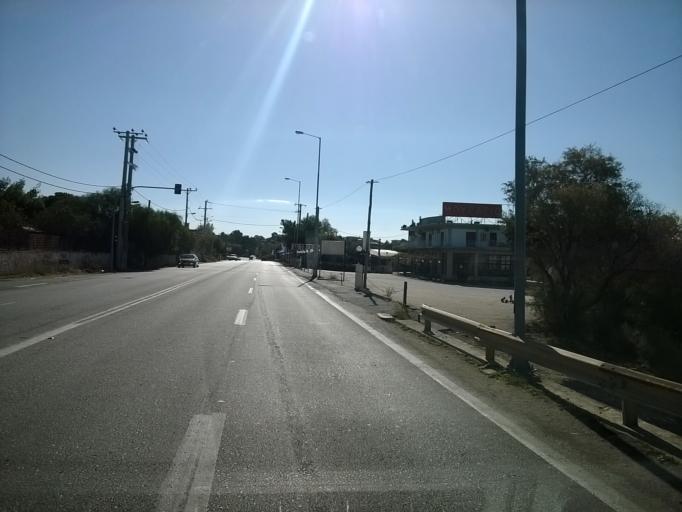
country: GR
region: Attica
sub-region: Nomarchia Anatolikis Attikis
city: Agios Dimitrios Kropias
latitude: 37.7991
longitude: 23.8705
